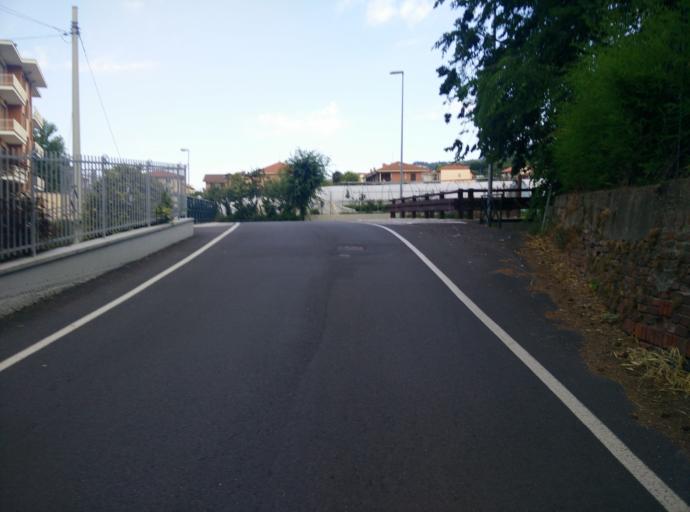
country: IT
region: Piedmont
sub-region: Provincia di Torino
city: Revigliasco
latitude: 44.9946
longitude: 7.7188
